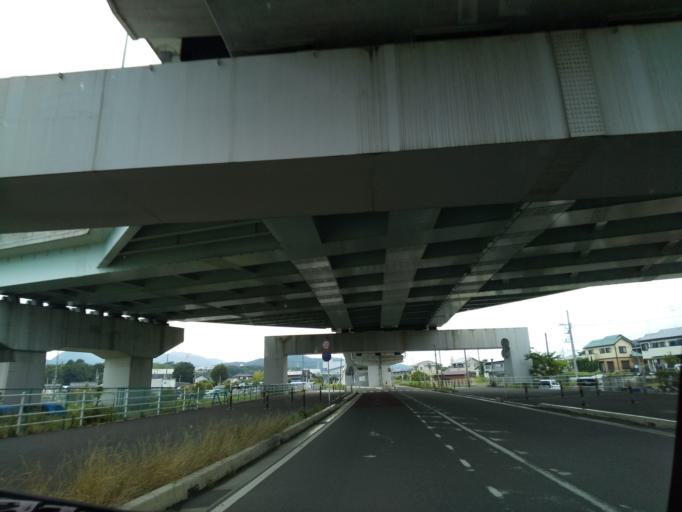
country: JP
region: Kanagawa
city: Zama
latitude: 35.4825
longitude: 139.3542
